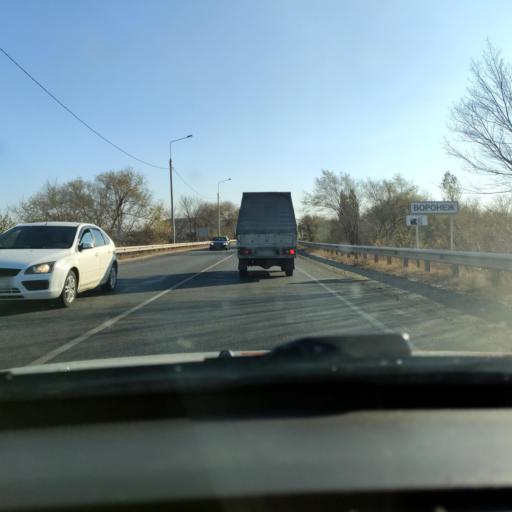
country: RU
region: Voronezj
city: Pridonskoy
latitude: 51.7151
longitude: 39.0748
